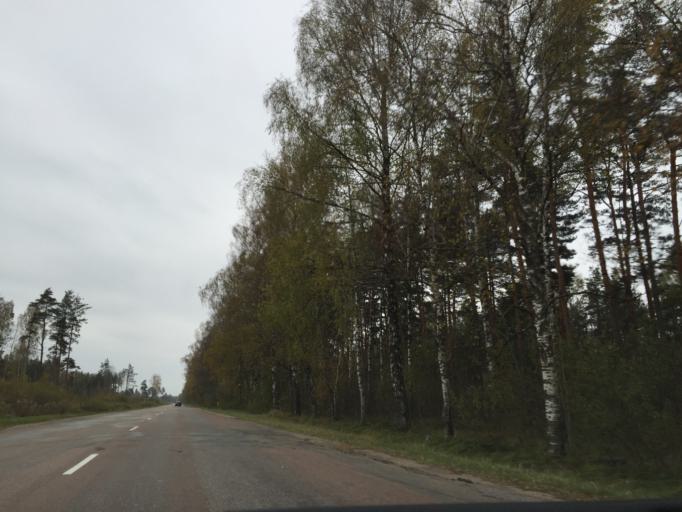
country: LV
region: Marupe
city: Marupe
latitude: 56.8691
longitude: 24.0628
